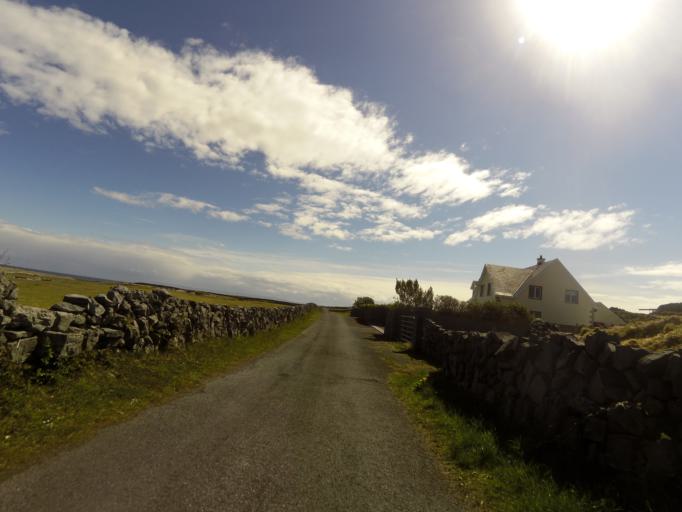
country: IE
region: Connaught
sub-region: County Galway
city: Oughterard
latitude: 53.0973
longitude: -9.6461
